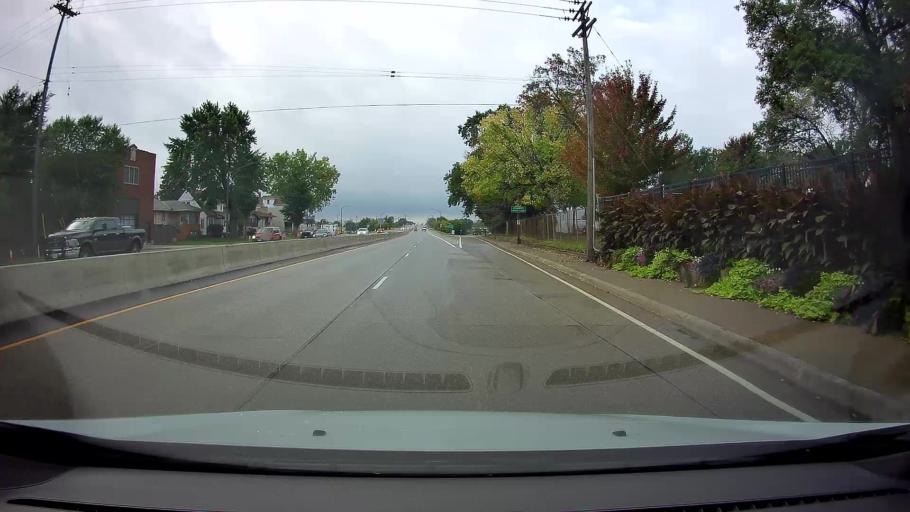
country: US
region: Minnesota
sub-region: Ramsey County
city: Falcon Heights
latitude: 44.9804
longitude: -93.1672
